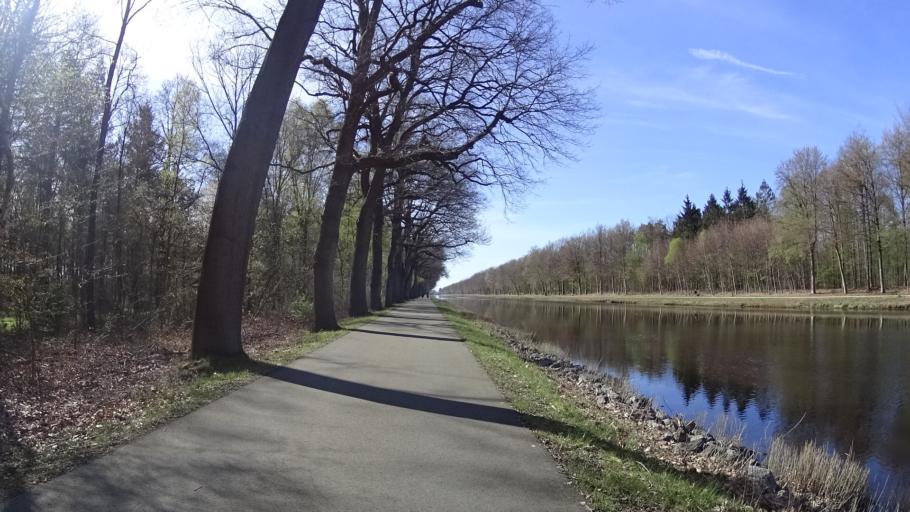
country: DE
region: Lower Saxony
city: Meppen
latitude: 52.6448
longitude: 7.3065
